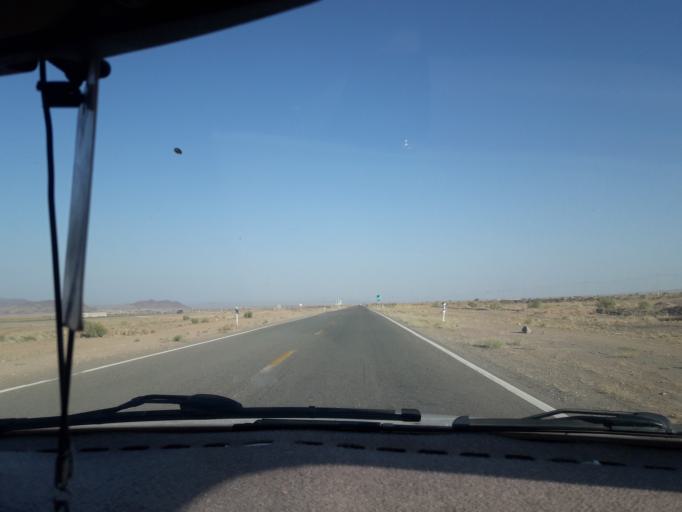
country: IR
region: Khorasan-e Jonubi
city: Asadiyeh
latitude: 32.9866
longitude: 59.8469
